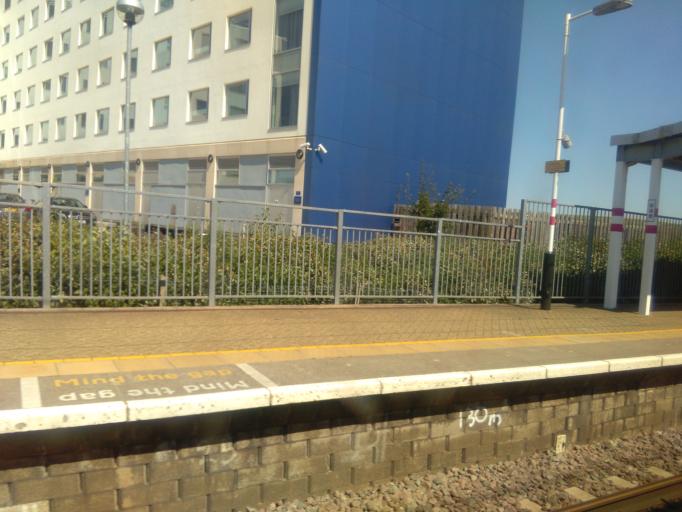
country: GB
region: England
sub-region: Luton
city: Luton
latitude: 51.8733
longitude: -0.3965
